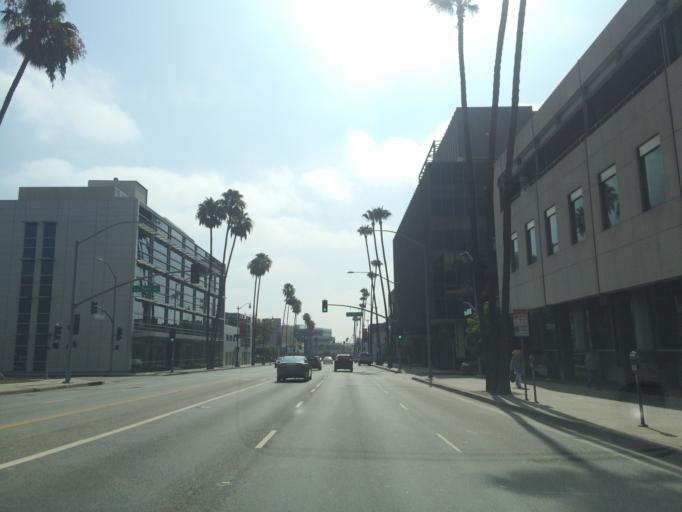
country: US
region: California
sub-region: Los Angeles County
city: Beverly Hills
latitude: 34.0670
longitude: -118.3874
